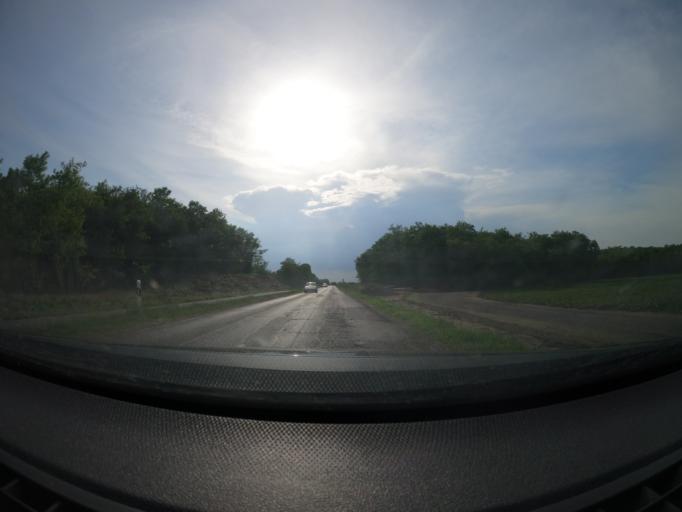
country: HU
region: Hajdu-Bihar
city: Vamospercs
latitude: 47.5267
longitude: 21.9311
